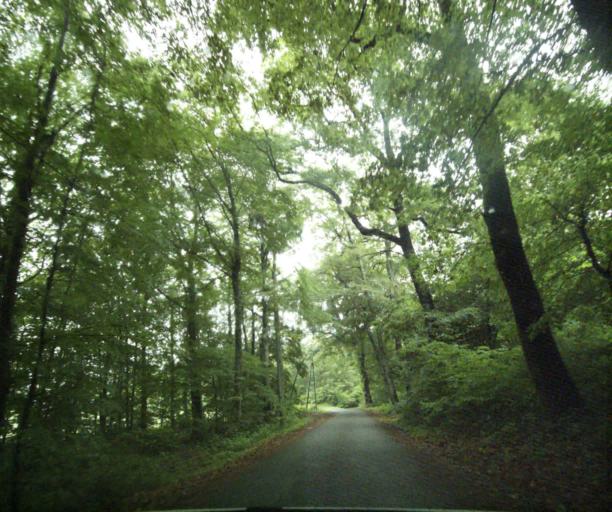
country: FR
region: Bourgogne
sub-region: Departement de Saone-et-Loire
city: Charolles
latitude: 46.4937
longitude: 4.4080
